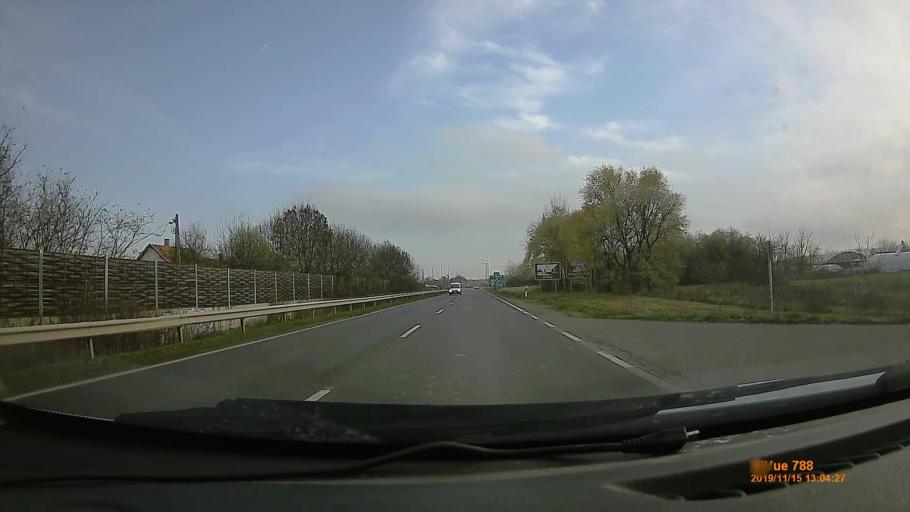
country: HU
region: Bekes
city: Gyula
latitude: 46.6352
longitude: 21.2542
